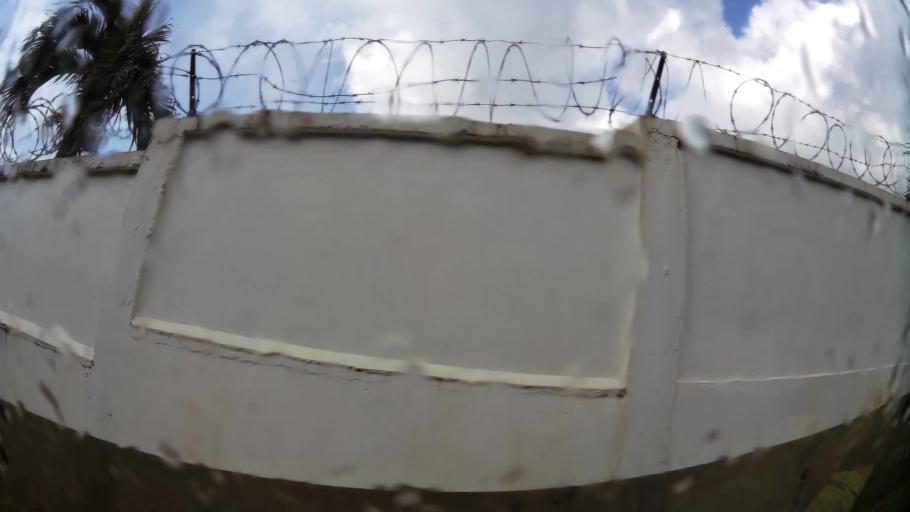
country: DM
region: Saint George
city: Roseau
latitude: 15.3228
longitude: -61.3909
